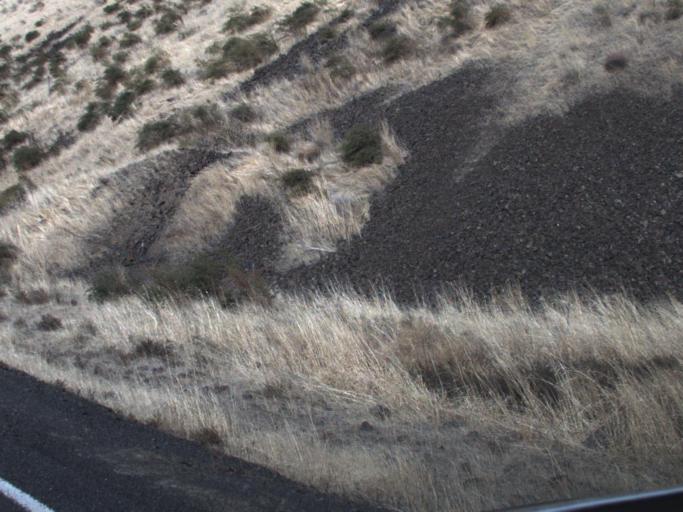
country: US
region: Washington
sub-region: Franklin County
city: Connell
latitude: 46.5952
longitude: -118.5474
